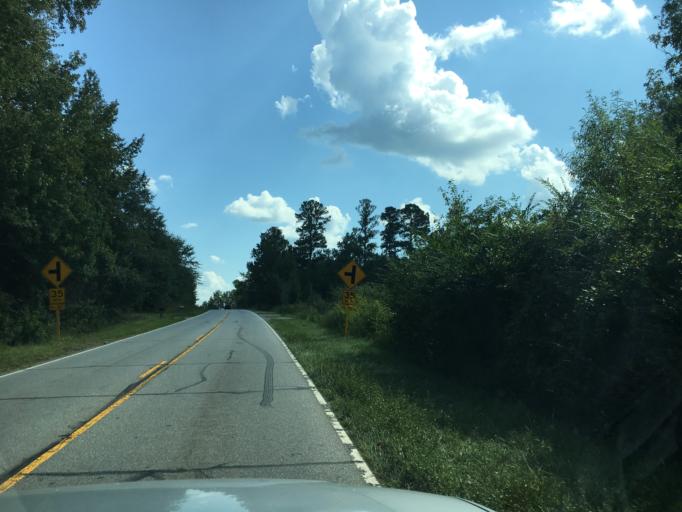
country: US
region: South Carolina
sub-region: Laurens County
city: Laurens
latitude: 34.5827
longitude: -82.0981
